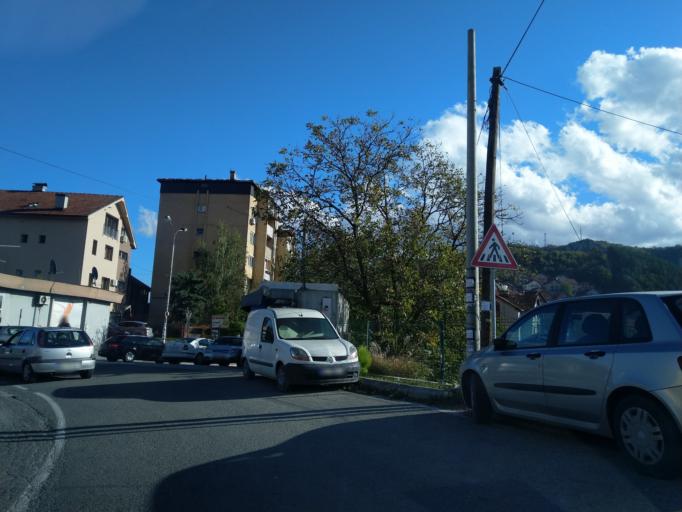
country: RS
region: Central Serbia
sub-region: Zlatiborski Okrug
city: Uzice
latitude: 43.8590
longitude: 19.8255
